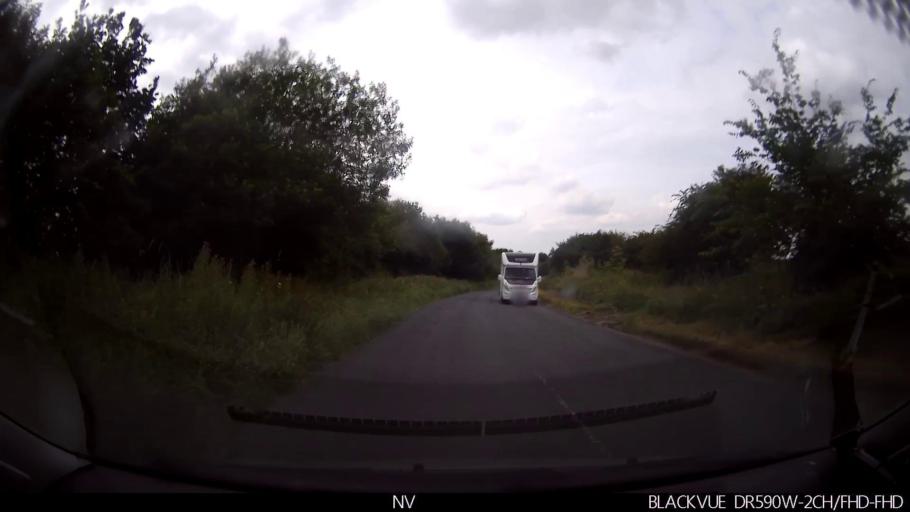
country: GB
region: England
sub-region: City of York
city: Holtby
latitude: 54.0429
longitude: -0.9577
